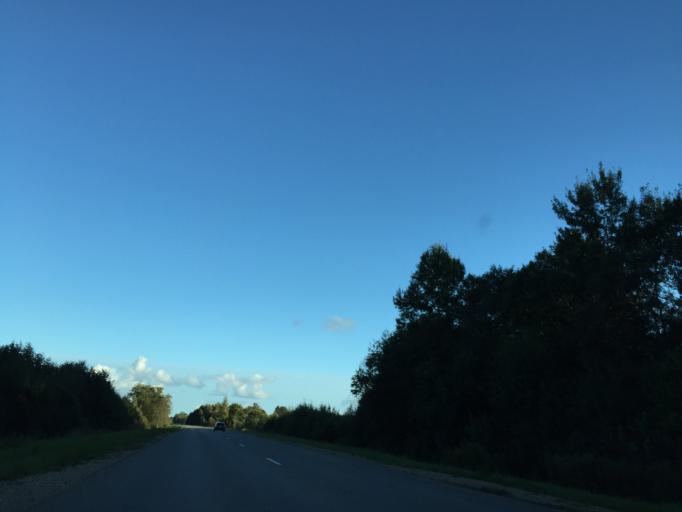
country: LV
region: Kuldigas Rajons
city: Kuldiga
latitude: 56.9494
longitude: 22.0142
